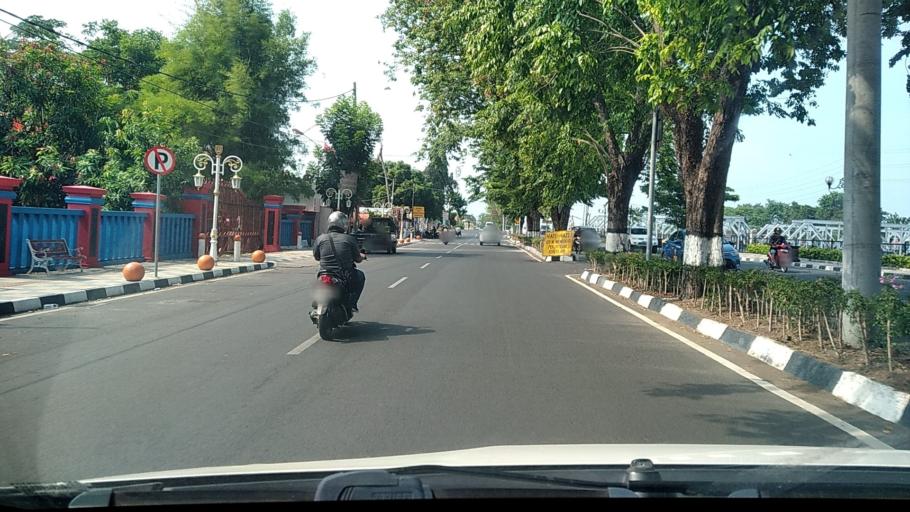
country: ID
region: Central Java
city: Semarang
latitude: -6.9788
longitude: 110.4011
